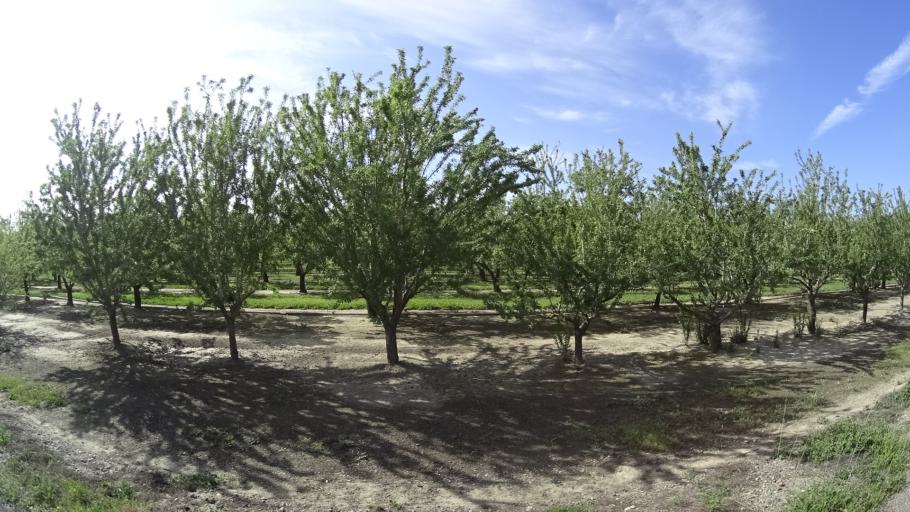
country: US
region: California
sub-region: Glenn County
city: Hamilton City
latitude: 39.6234
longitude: -122.0310
